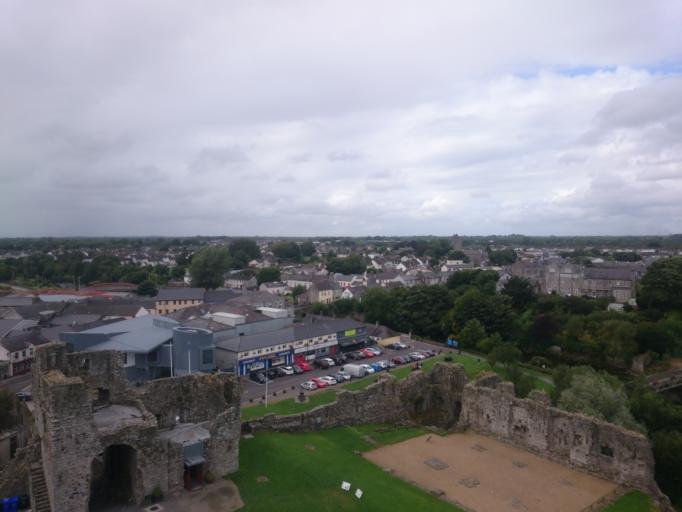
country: IE
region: Leinster
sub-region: An Mhi
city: Trim
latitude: 53.5544
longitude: -6.7897
